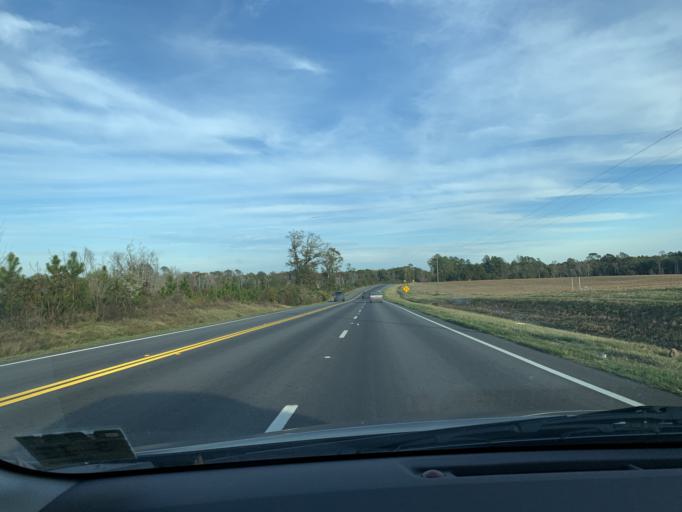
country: US
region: Georgia
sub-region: Irwin County
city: Ocilla
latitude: 31.5955
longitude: -83.1811
